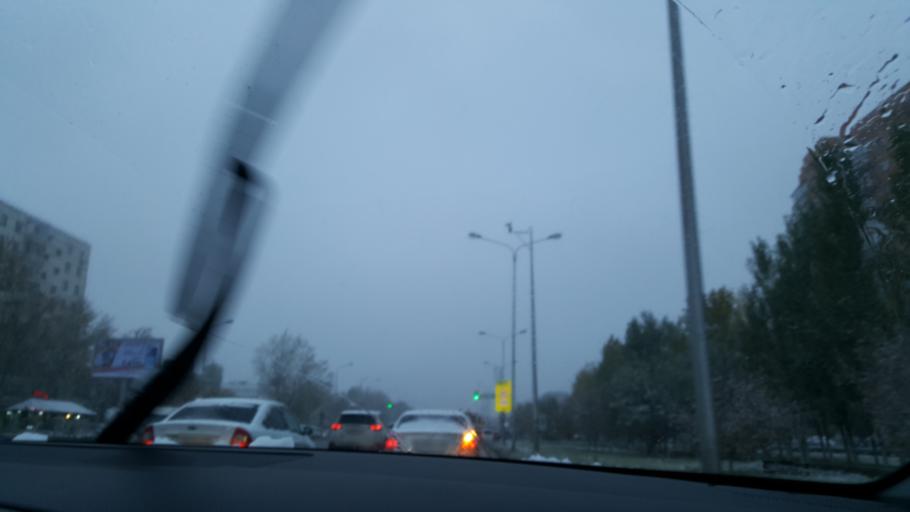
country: KZ
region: Astana Qalasy
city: Astana
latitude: 51.1539
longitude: 71.4879
